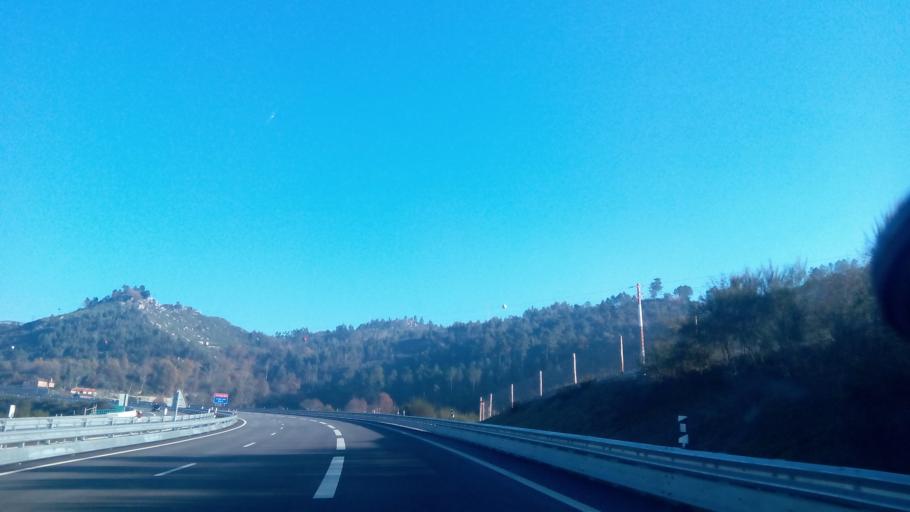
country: PT
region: Porto
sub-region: Amarante
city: Amarante
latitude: 41.2605
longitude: -8.0203
